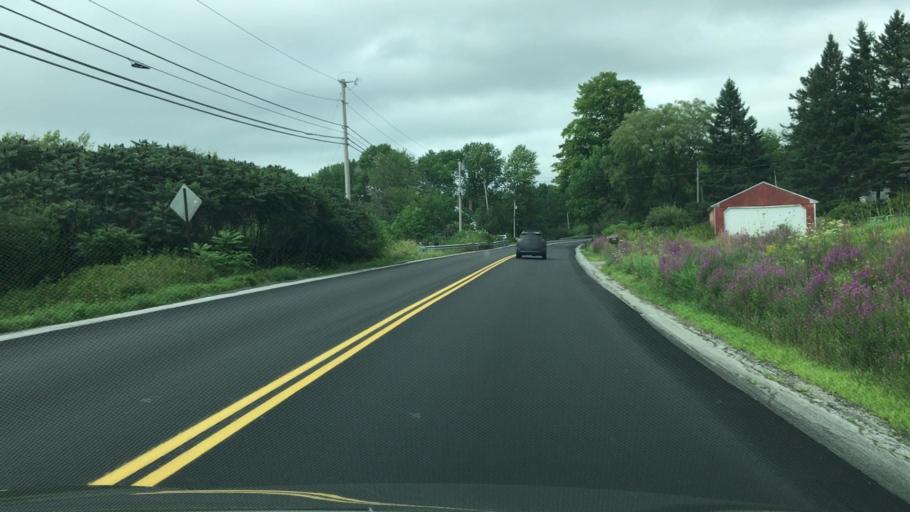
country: US
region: Maine
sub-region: Waldo County
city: Winterport
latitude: 44.6210
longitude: -68.8317
